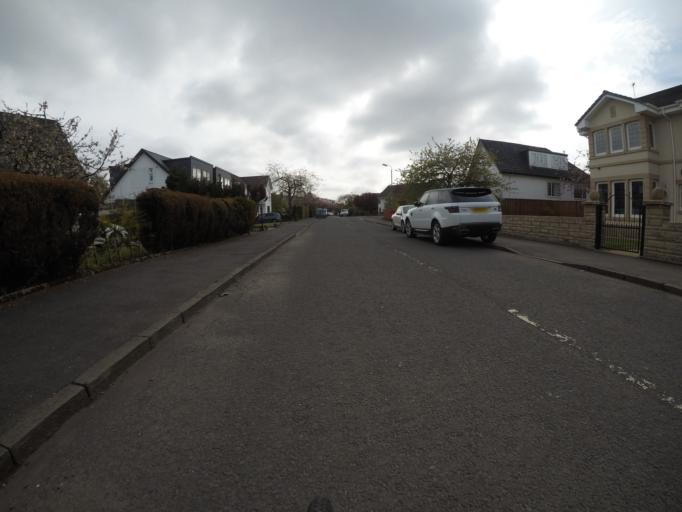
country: GB
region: Scotland
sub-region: East Renfrewshire
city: Busby
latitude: 55.7794
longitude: -4.3017
